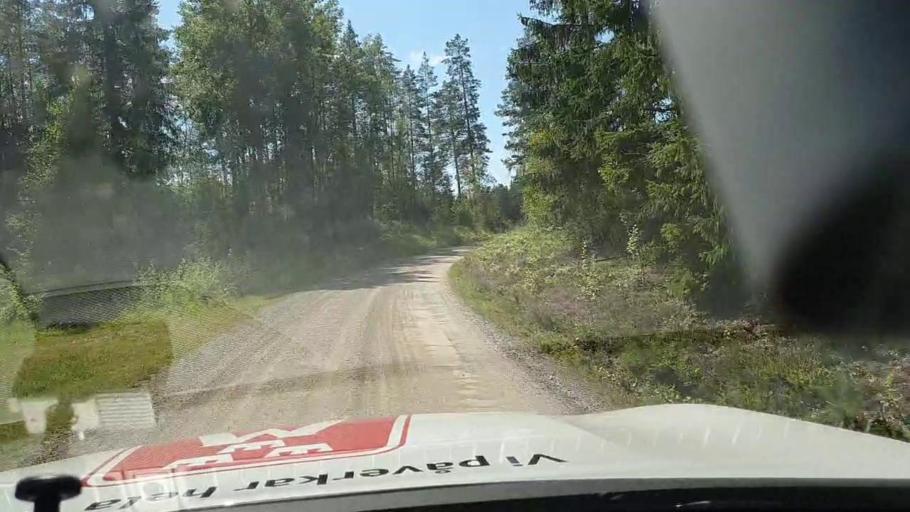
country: SE
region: Soedermanland
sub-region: Strangnas Kommun
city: Akers Styckebruk
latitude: 59.2000
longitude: 16.9188
